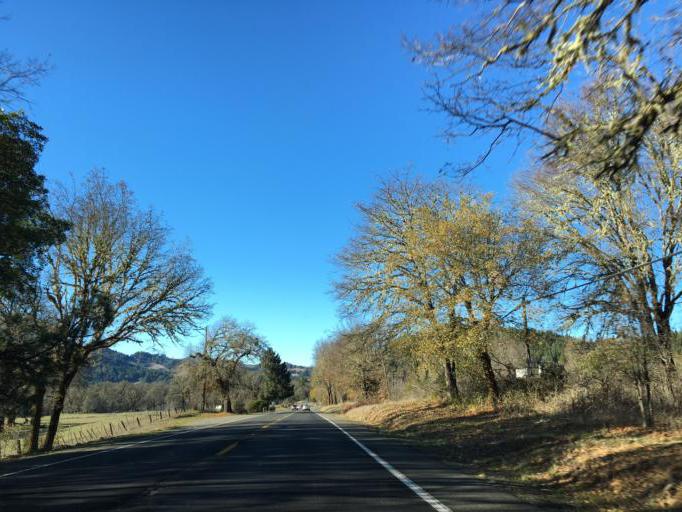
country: US
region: California
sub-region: Mendocino County
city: Laytonville
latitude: 39.7434
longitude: -123.5200
